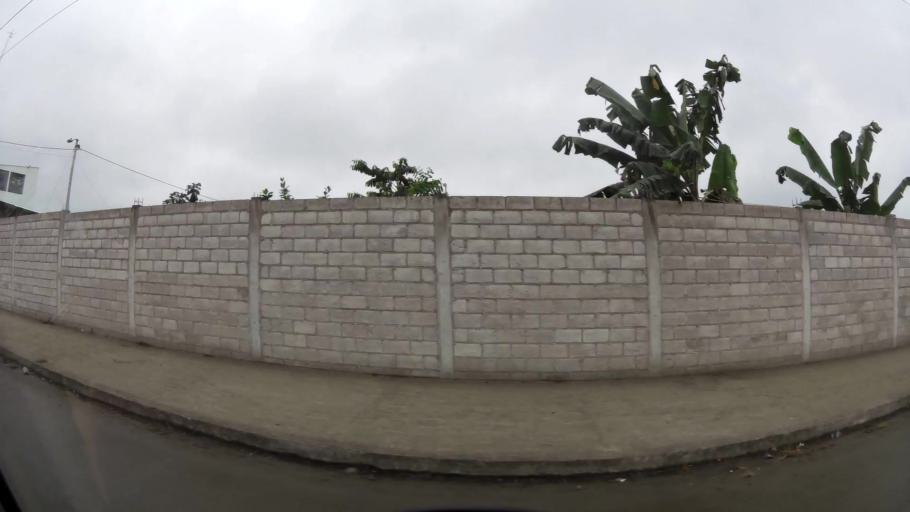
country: EC
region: El Oro
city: Pasaje
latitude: -3.3258
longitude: -79.8174
